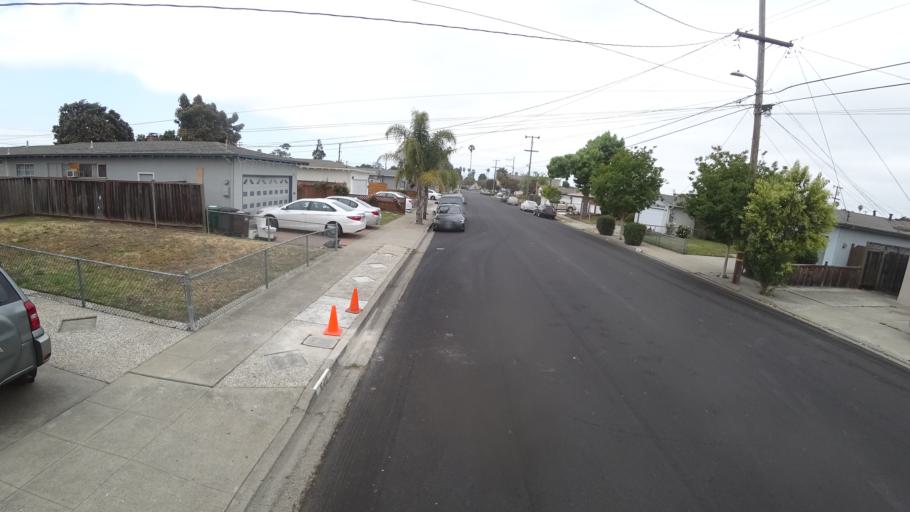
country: US
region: California
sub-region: Alameda County
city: Hayward
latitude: 37.6286
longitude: -122.0653
